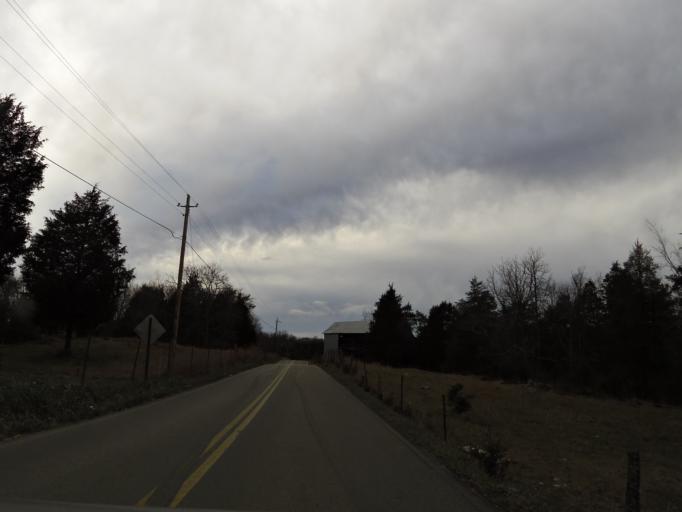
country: US
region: Tennessee
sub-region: Greene County
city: Tusculum
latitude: 36.2064
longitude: -82.7448
